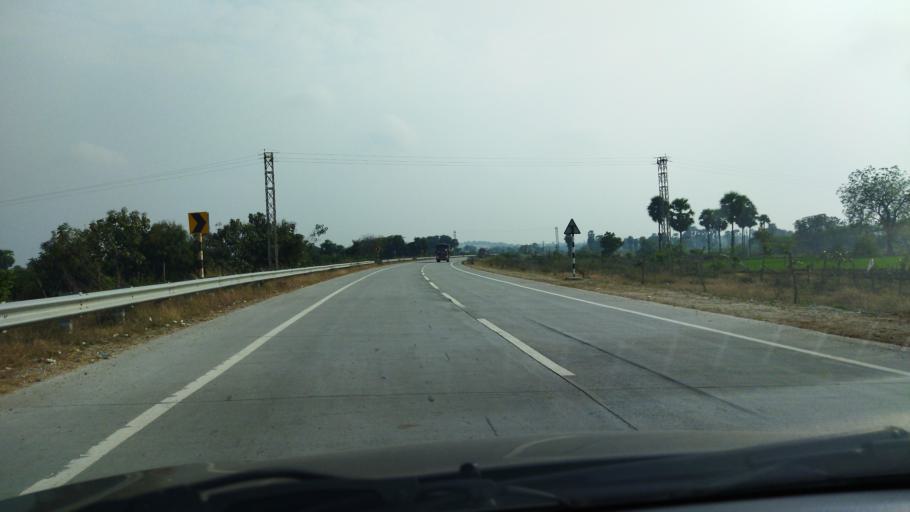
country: IN
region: Telangana
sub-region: Nalgonda
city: Nalgonda
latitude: 17.1752
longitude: 79.3979
